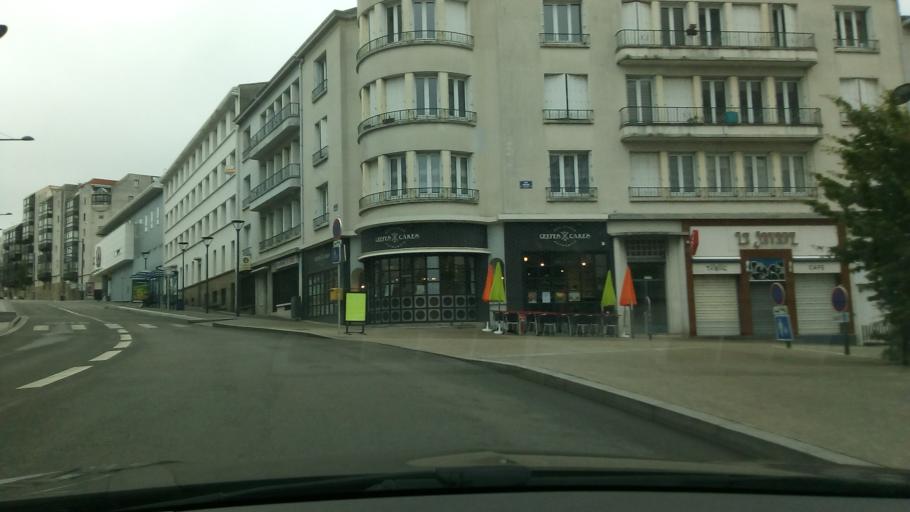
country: FR
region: Brittany
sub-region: Departement du Finistere
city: Brest
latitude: 48.3917
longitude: -4.4851
